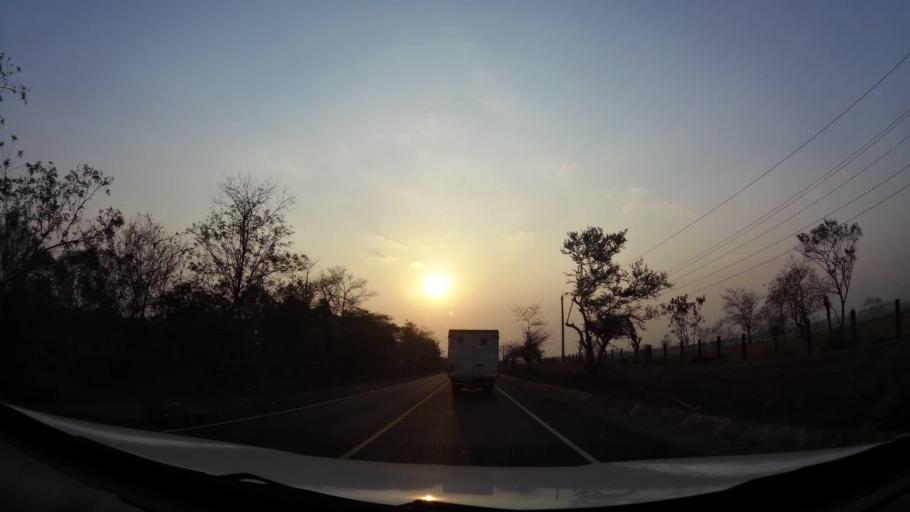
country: NI
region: Leon
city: La Paz Centro
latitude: 12.3301
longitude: -86.6425
